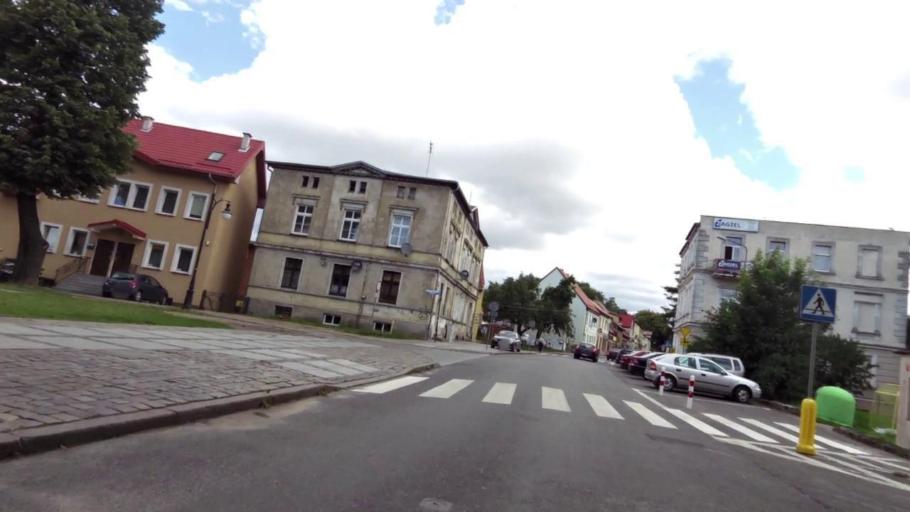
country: PL
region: West Pomeranian Voivodeship
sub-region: Powiat slawienski
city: Darlowo
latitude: 54.4232
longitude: 16.4126
